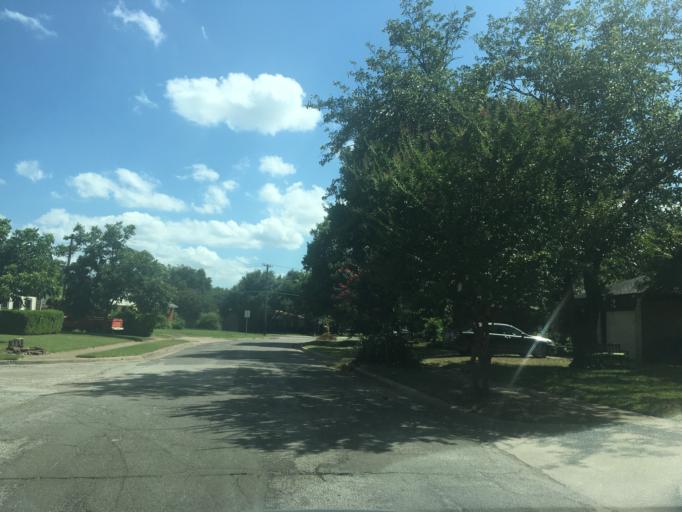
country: US
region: Texas
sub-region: Dallas County
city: Garland
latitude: 32.8343
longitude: -96.6809
